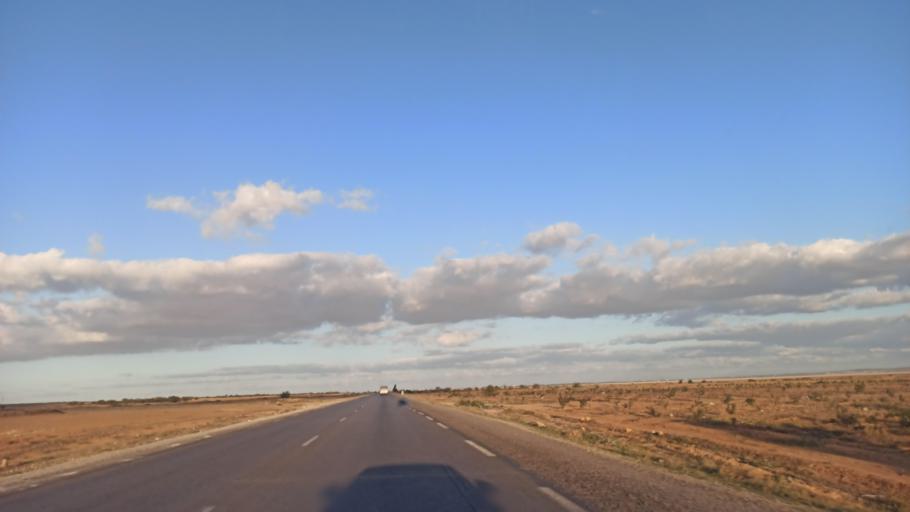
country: TN
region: Al Qayrawan
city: Sbikha
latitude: 35.8913
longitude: 10.2470
